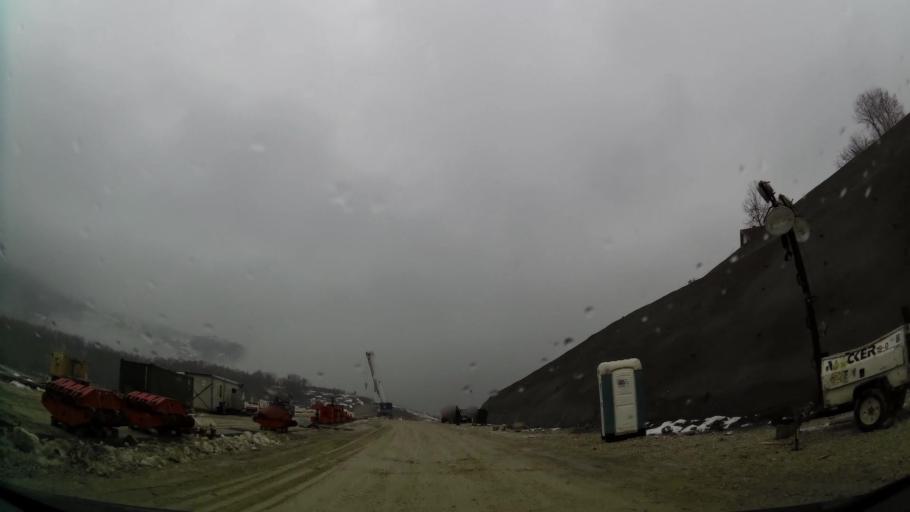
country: XK
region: Ferizaj
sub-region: Hani i Elezit
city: Hani i Elezit
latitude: 42.1661
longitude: 21.2828
